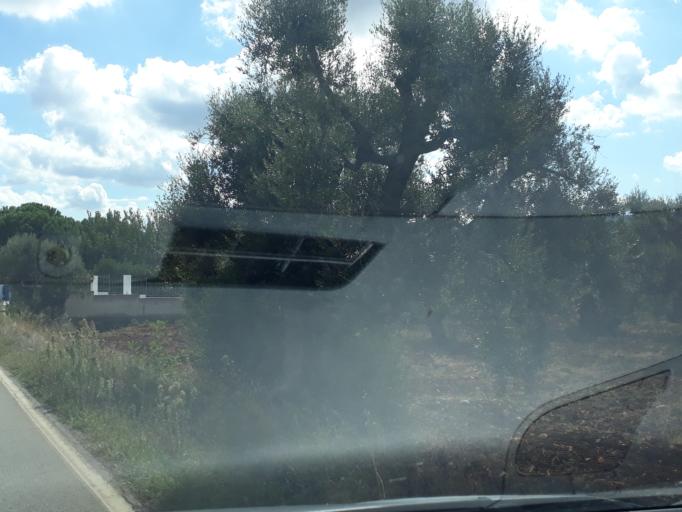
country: IT
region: Apulia
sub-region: Provincia di Brindisi
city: Fasano
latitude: 40.8248
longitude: 17.3711
